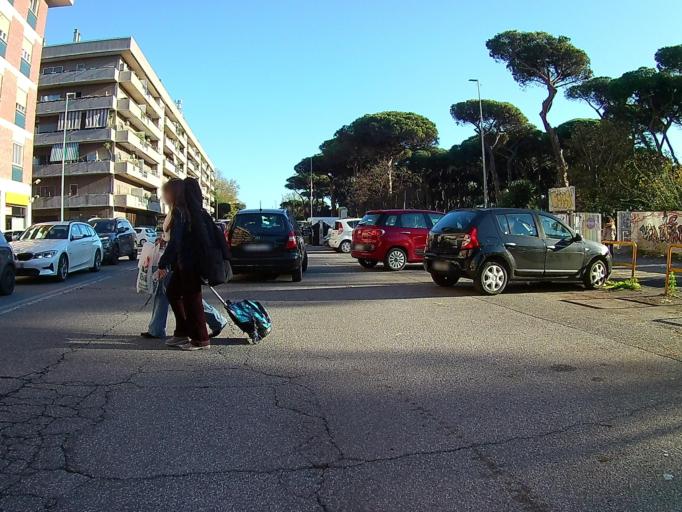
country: IT
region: Latium
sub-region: Citta metropolitana di Roma Capitale
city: Lido di Ostia
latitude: 41.7347
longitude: 12.2959
